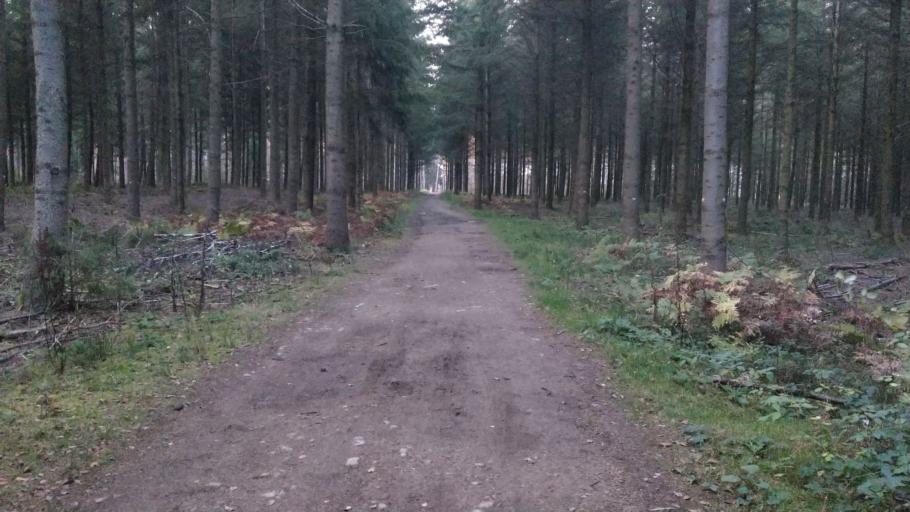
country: NL
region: Limburg
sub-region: Gemeente Vaals
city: Vaals
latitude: 50.7493
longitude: 6.0250
